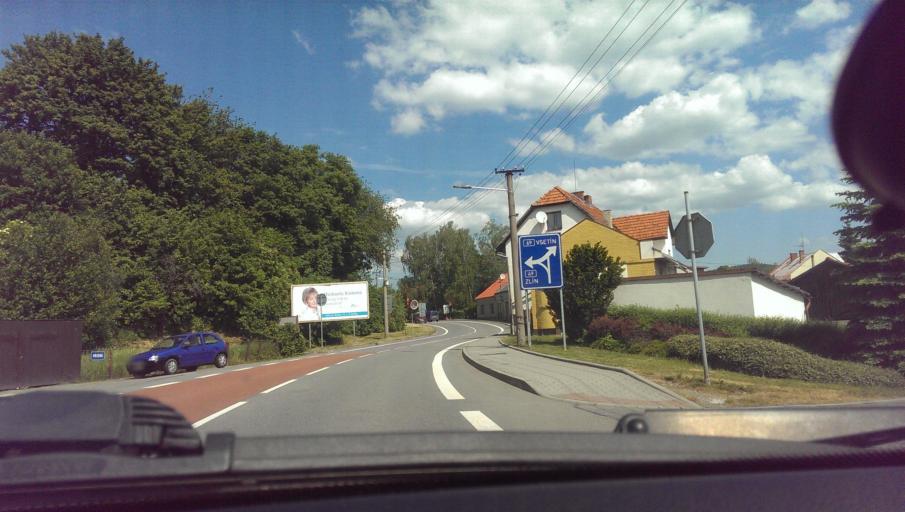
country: CZ
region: Zlin
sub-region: Okres Zlin
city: Vizovice
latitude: 49.2175
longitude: 17.8537
